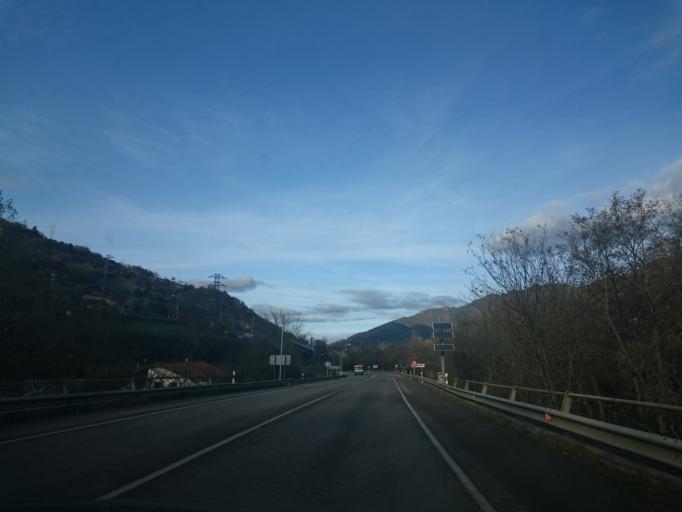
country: ES
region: Asturias
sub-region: Province of Asturias
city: Pola de Lena
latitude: 43.1077
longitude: -5.8186
